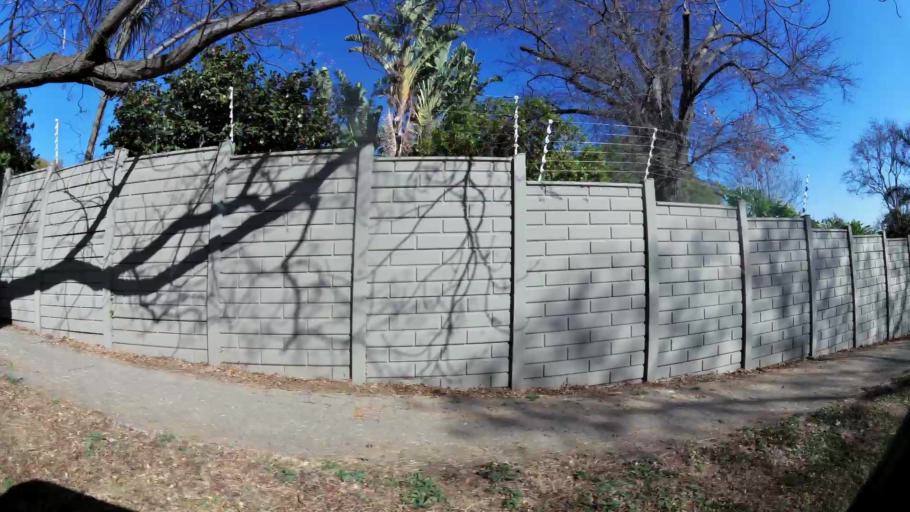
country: ZA
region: Gauteng
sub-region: City of Johannesburg Metropolitan Municipality
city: Johannesburg
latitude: -26.1202
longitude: 28.0240
